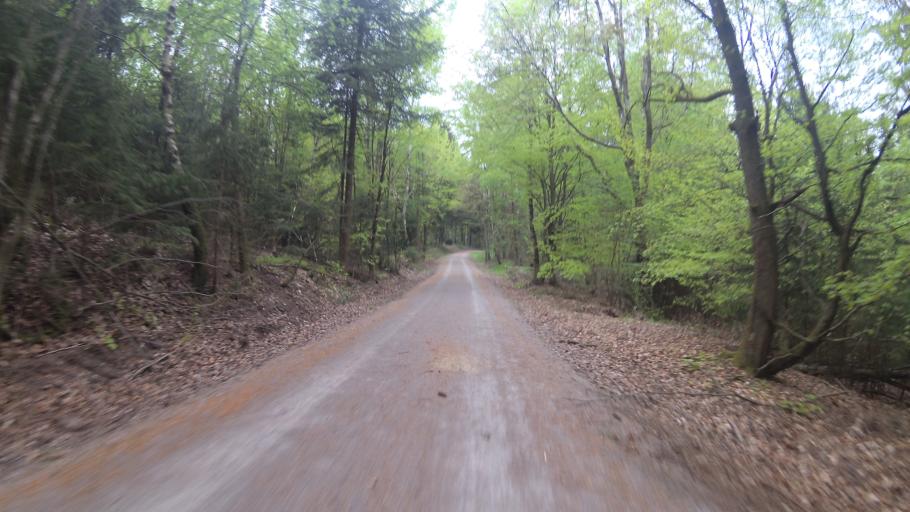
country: DE
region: Saarland
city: Mainzweiler
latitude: 49.4018
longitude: 7.1219
